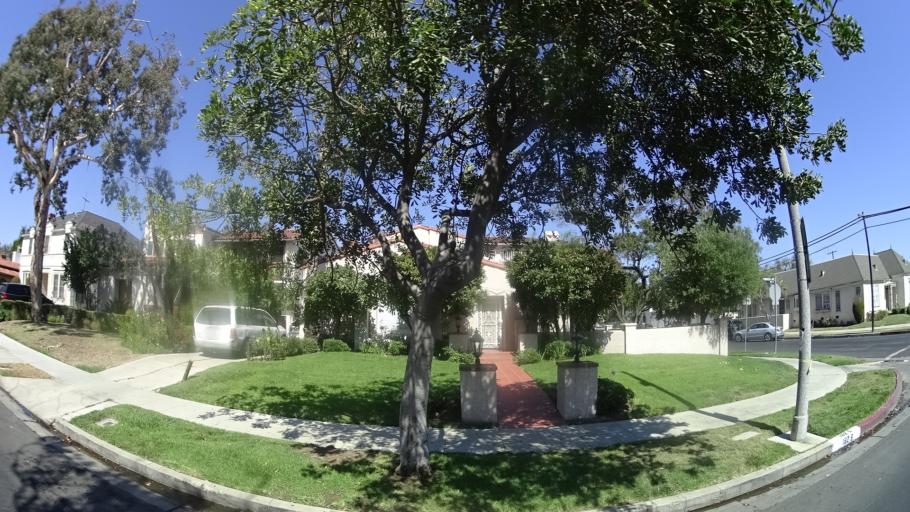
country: US
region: California
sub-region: Los Angeles County
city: West Hollywood
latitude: 34.0711
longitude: -118.3462
